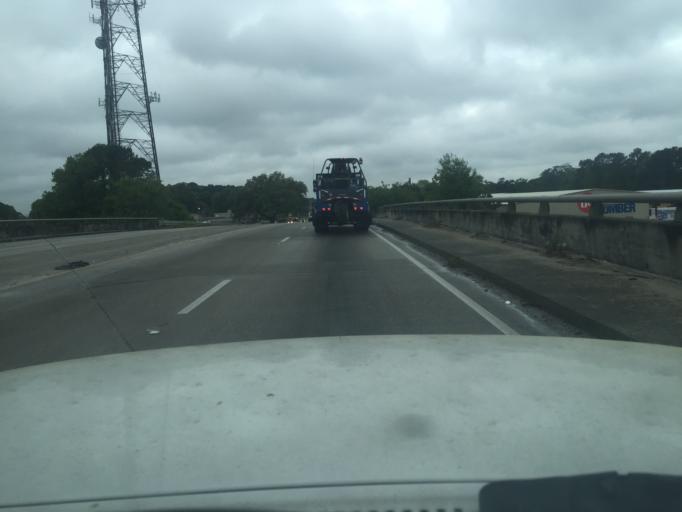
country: US
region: Georgia
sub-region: Chatham County
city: Garden City
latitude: 32.0503
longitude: -81.1571
